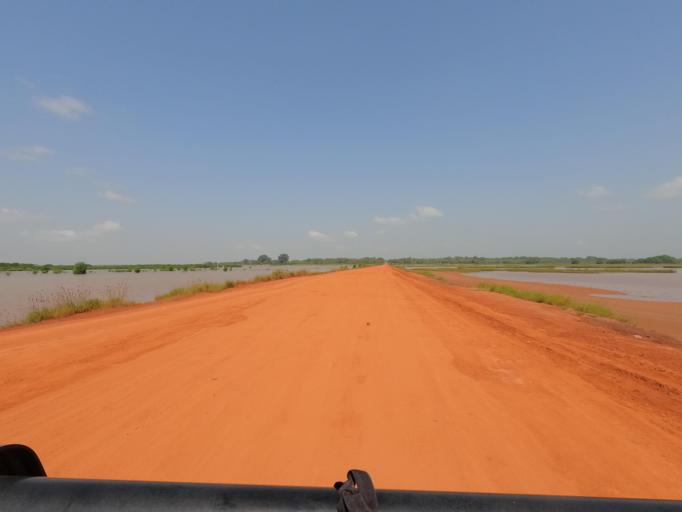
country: GW
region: Cacheu
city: Canchungo
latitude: 12.2581
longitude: -15.7814
